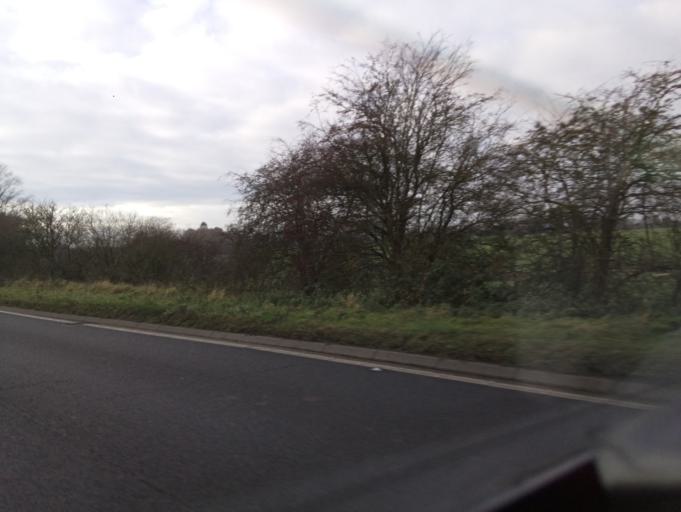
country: GB
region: England
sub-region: Staffordshire
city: Lichfield
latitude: 52.6556
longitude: -1.8098
